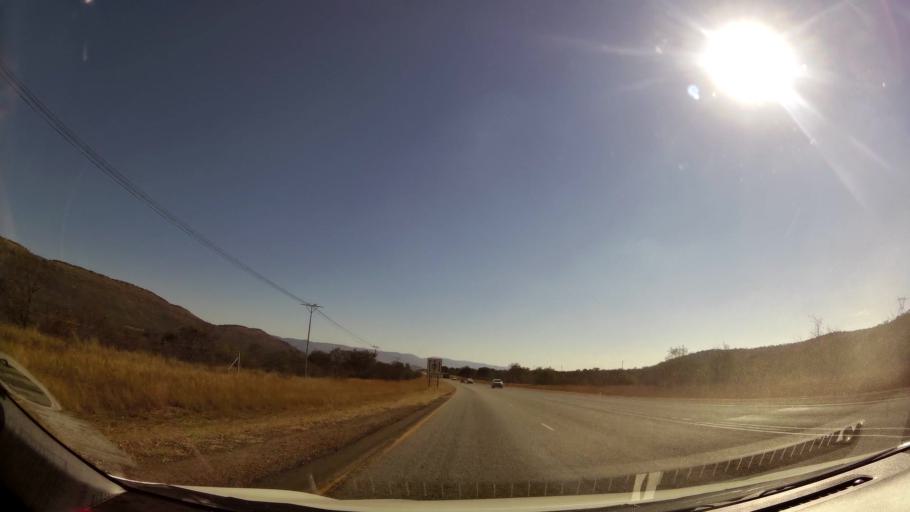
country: ZA
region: Limpopo
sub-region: Waterberg District Municipality
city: Mokopane
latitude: -24.1647
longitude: 29.0723
